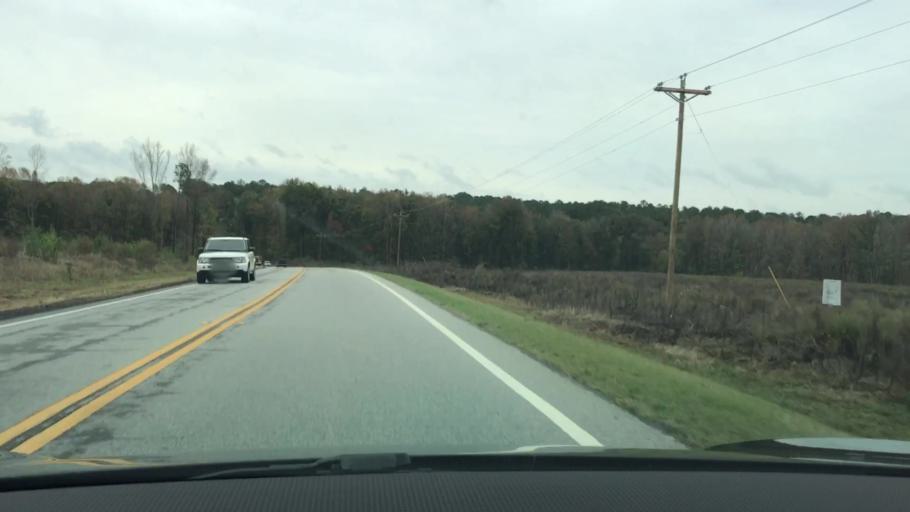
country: US
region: Georgia
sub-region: Greene County
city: Greensboro
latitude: 33.6127
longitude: -83.2082
